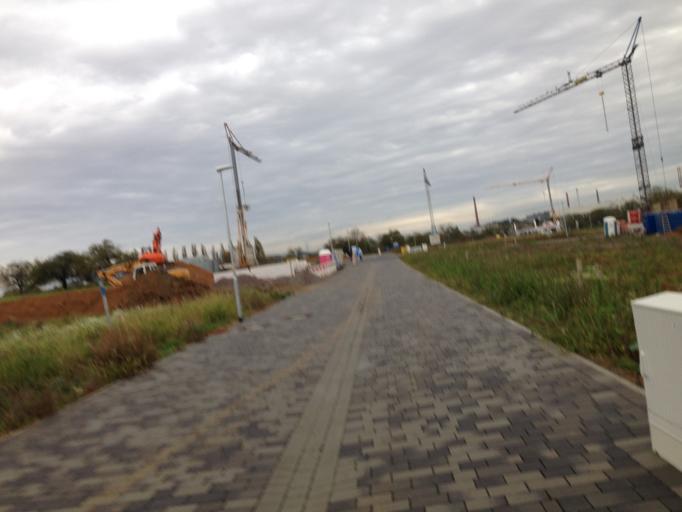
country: DE
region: Hesse
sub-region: Regierungsbezirk Giessen
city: Heuchelheim
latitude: 50.5878
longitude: 8.6243
